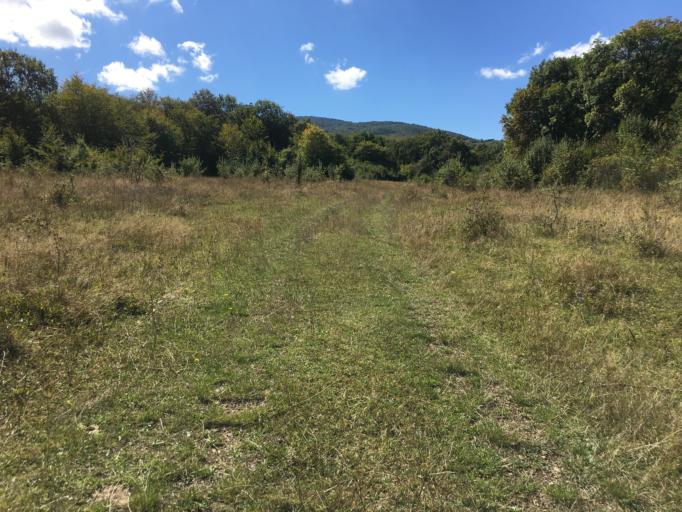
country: GE
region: Mtskheta-Mtianeti
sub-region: Tianetis Munitsip'alit'et'i
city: T'ianet'i
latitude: 41.9338
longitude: 44.9754
